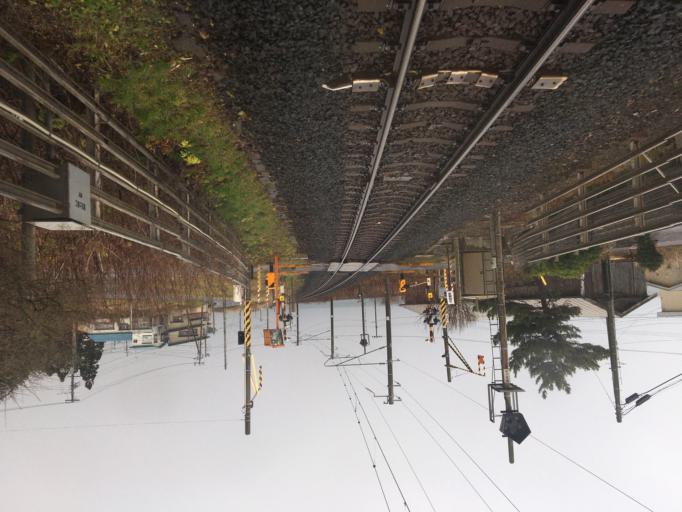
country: JP
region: Aomori
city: Aomori Shi
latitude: 41.0363
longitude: 140.6447
